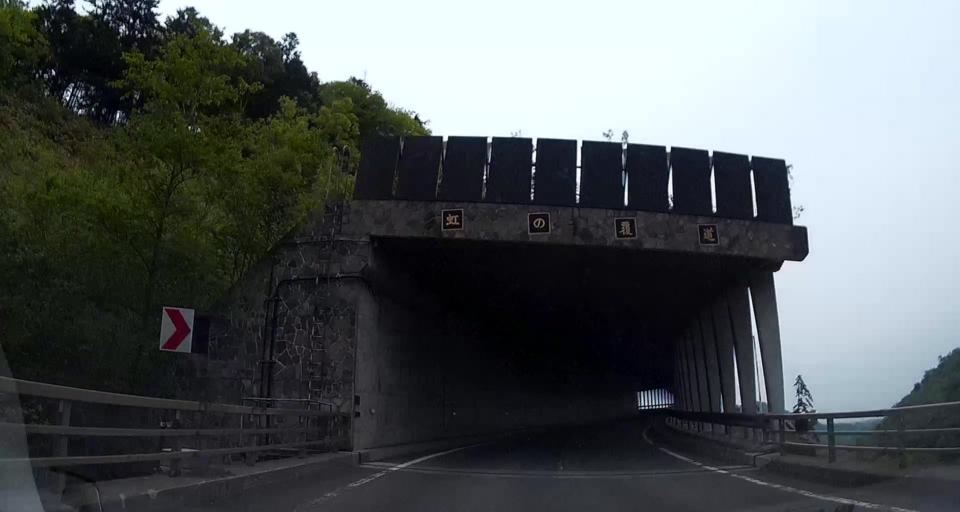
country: JP
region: Hokkaido
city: Shiraoi
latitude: 42.6578
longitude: 141.1733
